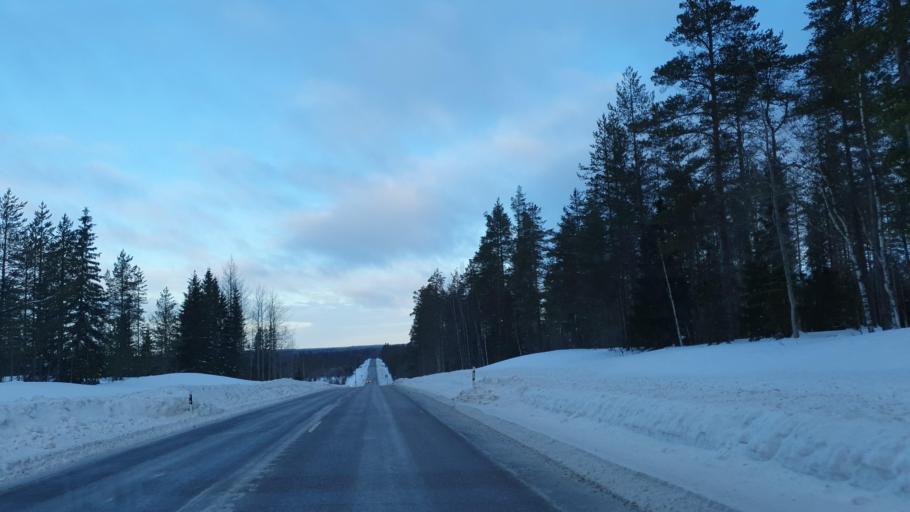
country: FI
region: Kainuu
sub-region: Kajaani
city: Kajaani
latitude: 64.4525
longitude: 27.5028
